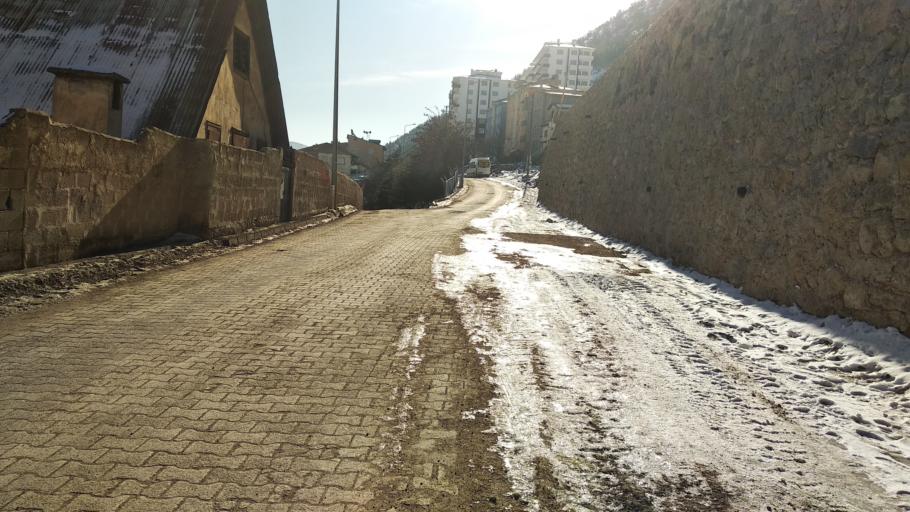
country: TR
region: Gumushane
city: Gumushkhane
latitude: 40.4564
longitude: 39.4870
